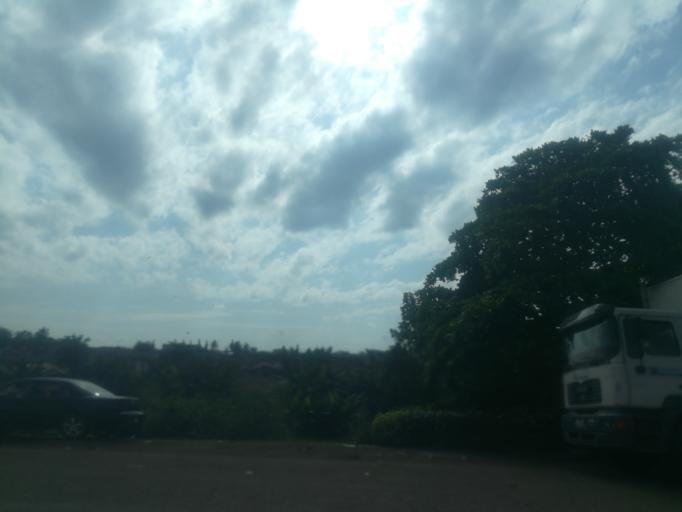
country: NG
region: Oyo
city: Ibadan
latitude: 7.3894
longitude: 3.9358
